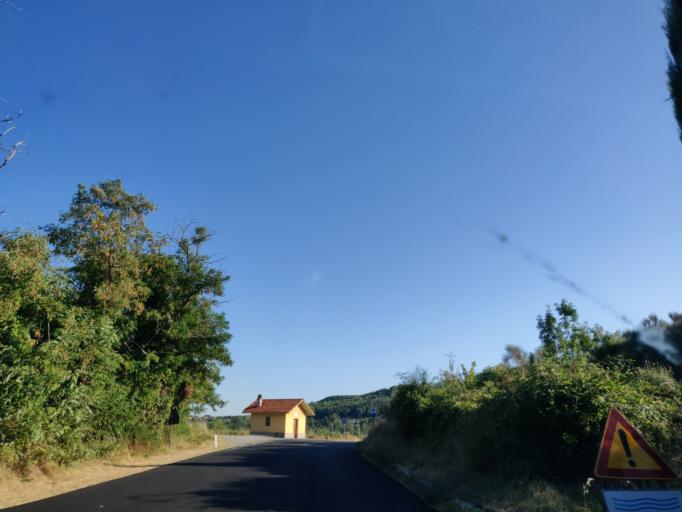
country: IT
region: Tuscany
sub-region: Provincia di Siena
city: Abbadia San Salvatore
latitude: 42.8679
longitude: 11.6814
